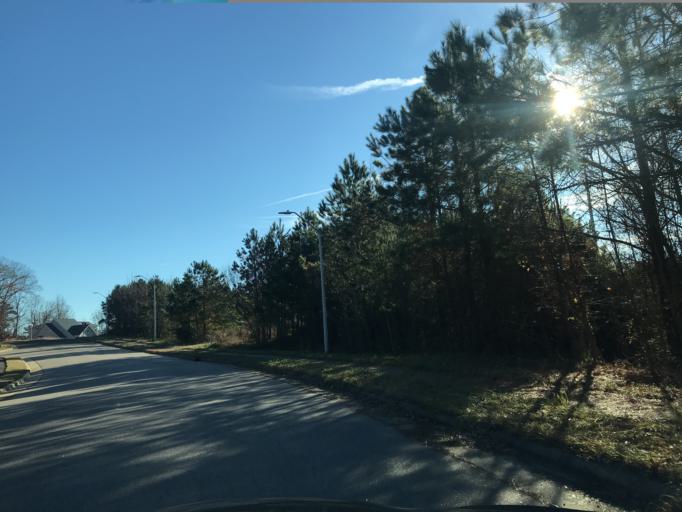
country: US
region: North Carolina
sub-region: Wake County
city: West Raleigh
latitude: 35.8969
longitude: -78.6057
